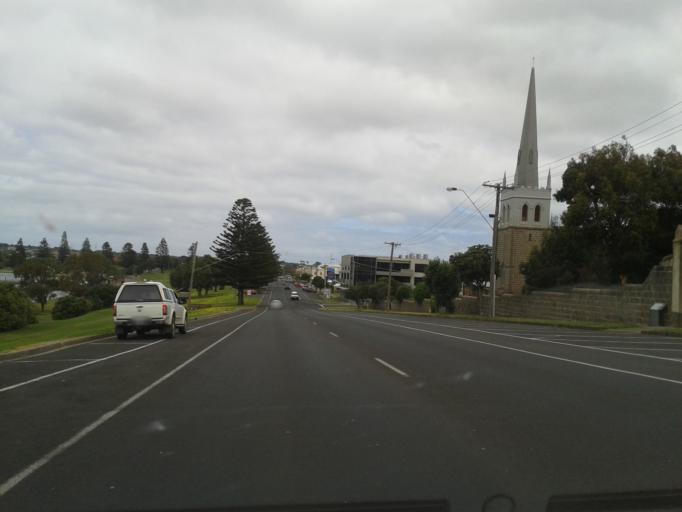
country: AU
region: Victoria
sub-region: Glenelg
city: Portland
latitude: -38.3451
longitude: 141.6065
